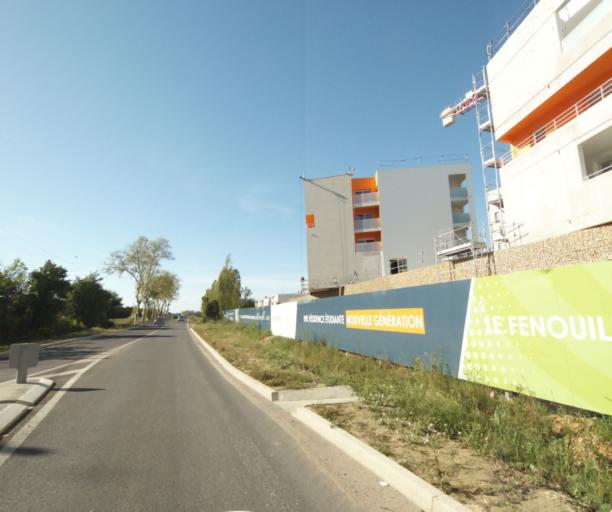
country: FR
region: Languedoc-Roussillon
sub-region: Departement de l'Herault
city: Perols
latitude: 43.5749
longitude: 3.9356
